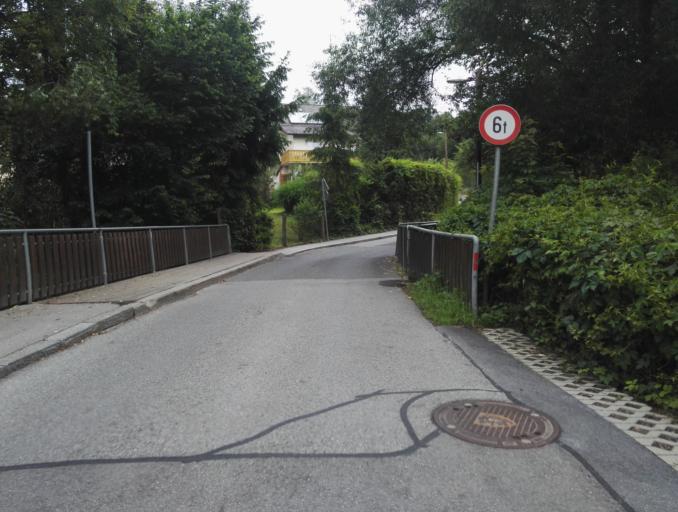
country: AT
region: Styria
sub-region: Graz Stadt
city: Mariatrost
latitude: 47.0753
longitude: 15.5001
